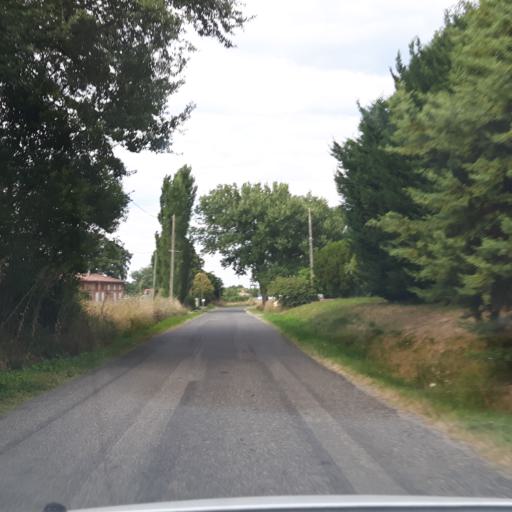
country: FR
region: Midi-Pyrenees
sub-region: Departement de la Haute-Garonne
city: Fronton
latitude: 43.8222
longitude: 1.3642
